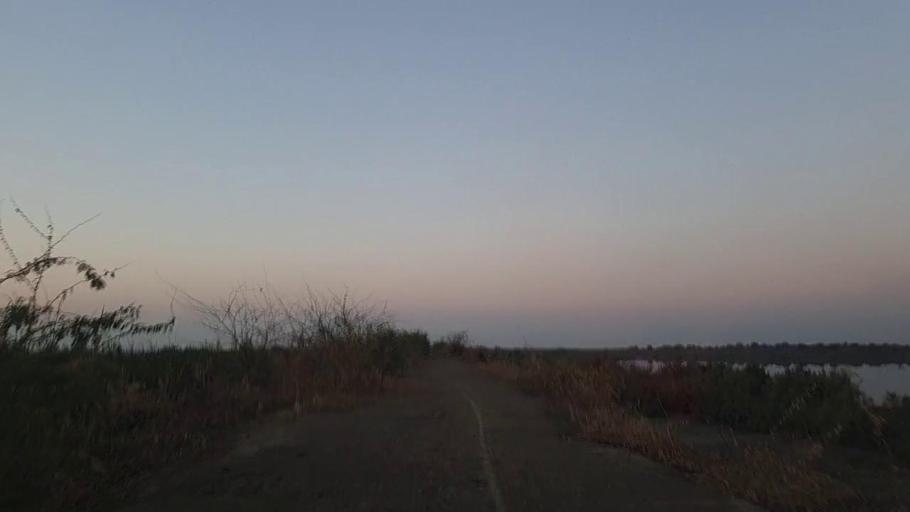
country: PK
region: Sindh
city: Tando Mittha Khan
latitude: 26.0794
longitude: 69.1525
